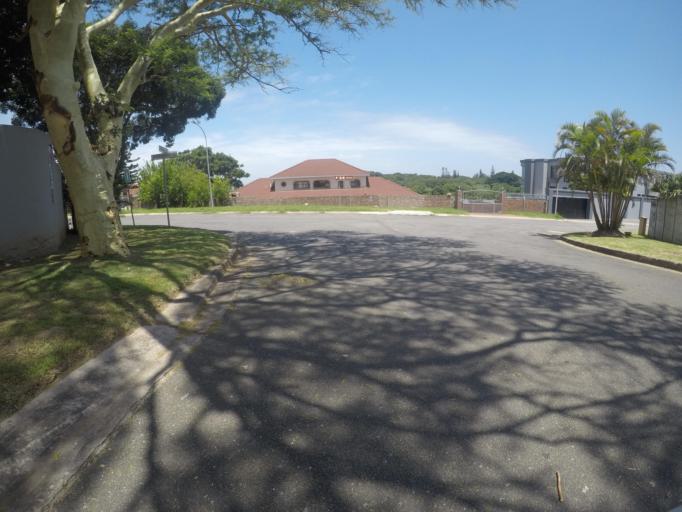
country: ZA
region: Eastern Cape
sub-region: Buffalo City Metropolitan Municipality
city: East London
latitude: -33.0042
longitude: 27.9229
